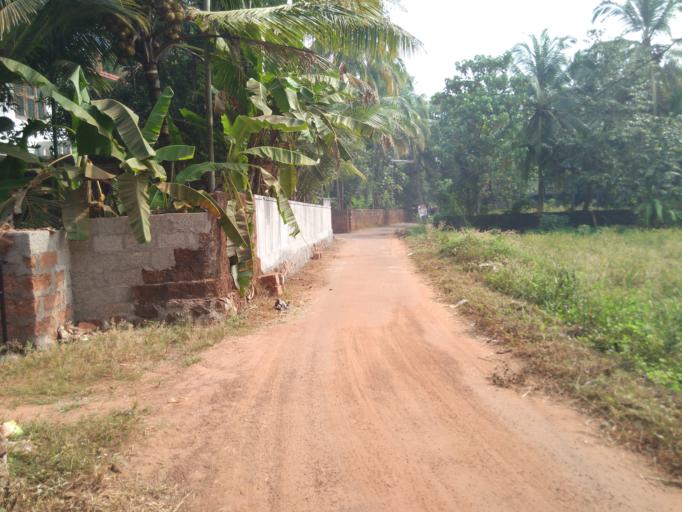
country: IN
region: Kerala
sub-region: Kozhikode
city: Kunnamangalam
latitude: 11.2885
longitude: 75.8347
